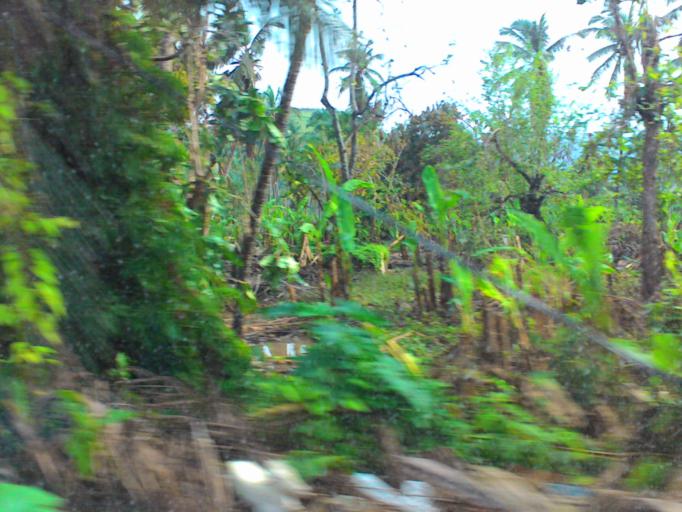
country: HT
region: Sud
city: Saint-Louis du Sud
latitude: 18.2697
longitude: -73.5964
